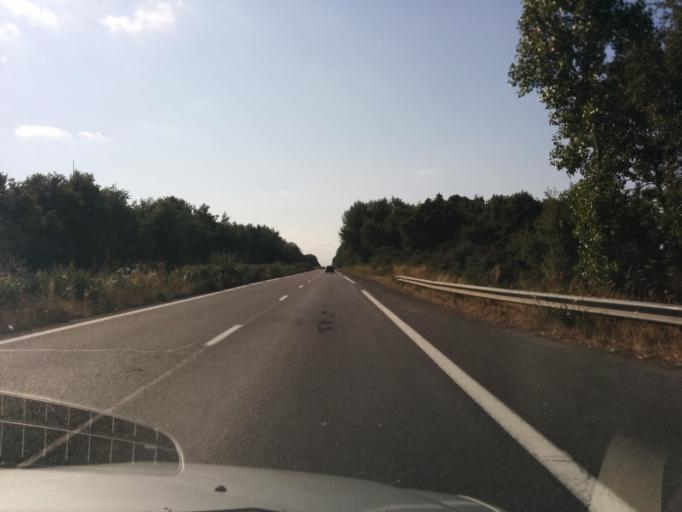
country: FR
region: Pays de la Loire
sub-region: Departement de la Loire-Atlantique
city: Haute-Goulaine
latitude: 47.1847
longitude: -1.4186
